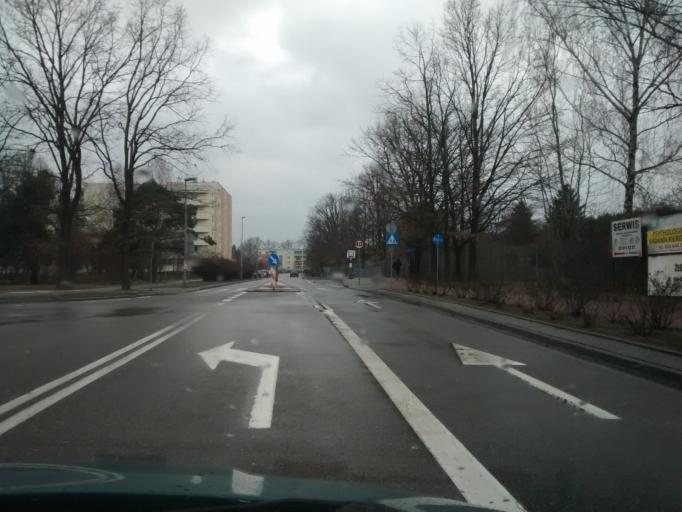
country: PL
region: Masovian Voivodeship
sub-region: Warszawa
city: Bialoleka
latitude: 52.3242
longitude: 20.9602
